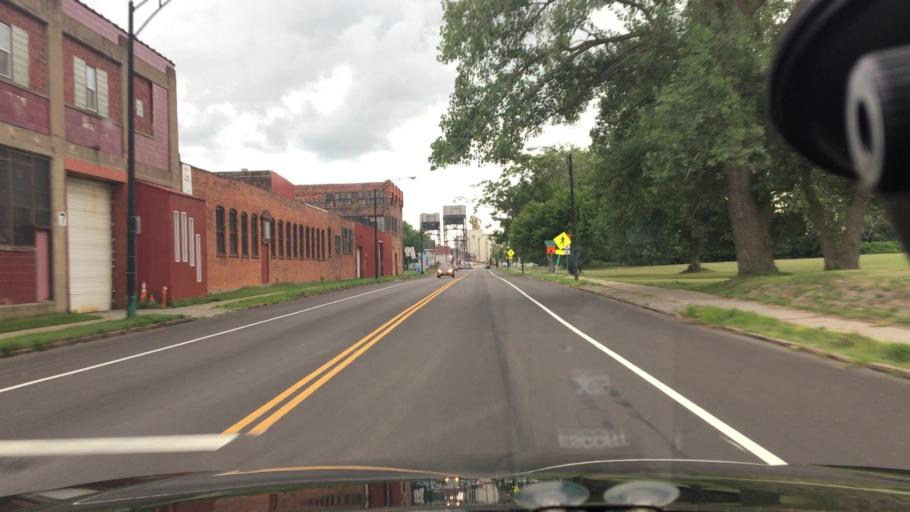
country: US
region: New York
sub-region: Erie County
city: Buffalo
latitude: 42.8682
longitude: -78.8657
